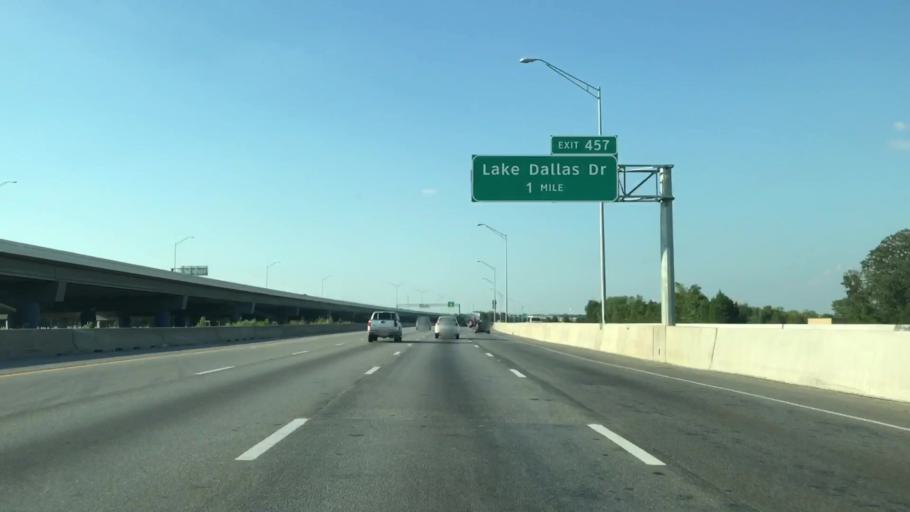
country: US
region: Texas
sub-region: Denton County
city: Highland Village
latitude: 33.0921
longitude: -97.0281
